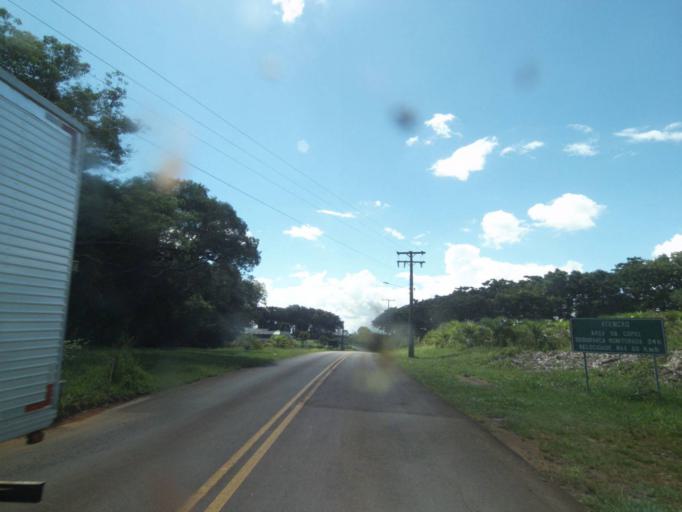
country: BR
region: Parana
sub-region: Pinhao
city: Pinhao
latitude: -25.7937
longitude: -52.0786
